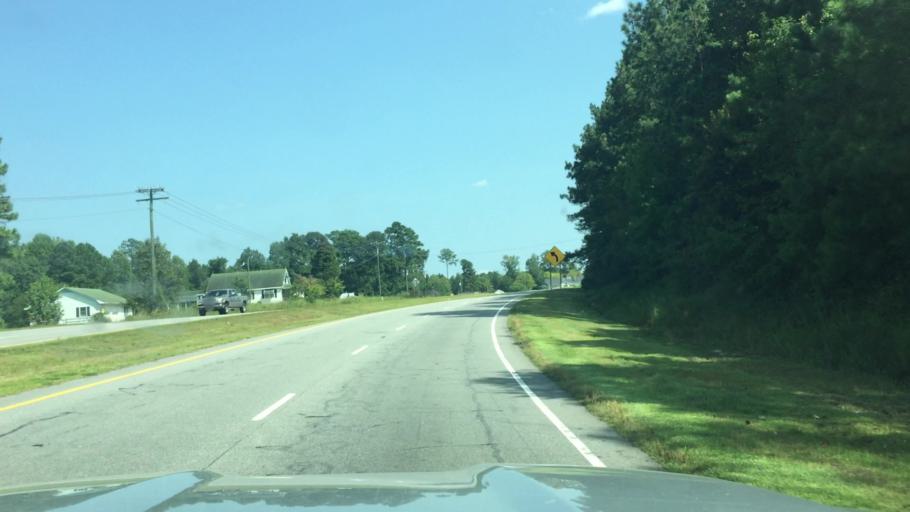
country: US
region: North Carolina
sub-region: Martin County
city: Williamston
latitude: 35.8122
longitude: -76.9296
